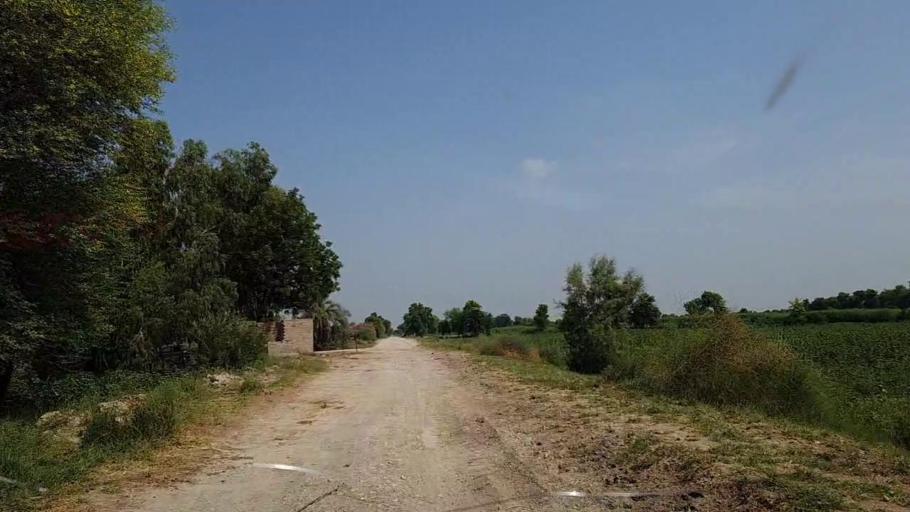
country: PK
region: Sindh
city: Adilpur
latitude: 27.8350
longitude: 69.2849
